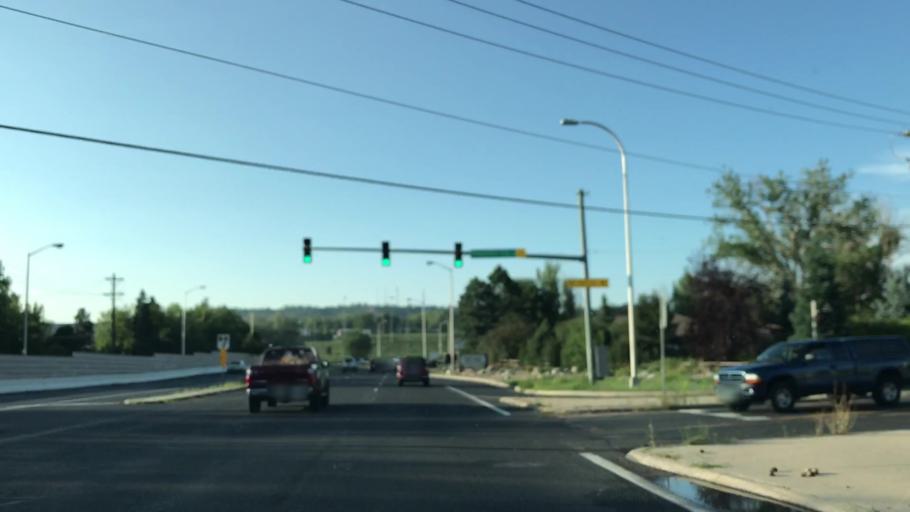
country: US
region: Colorado
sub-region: El Paso County
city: Colorado Springs
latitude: 38.8772
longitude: -104.7951
